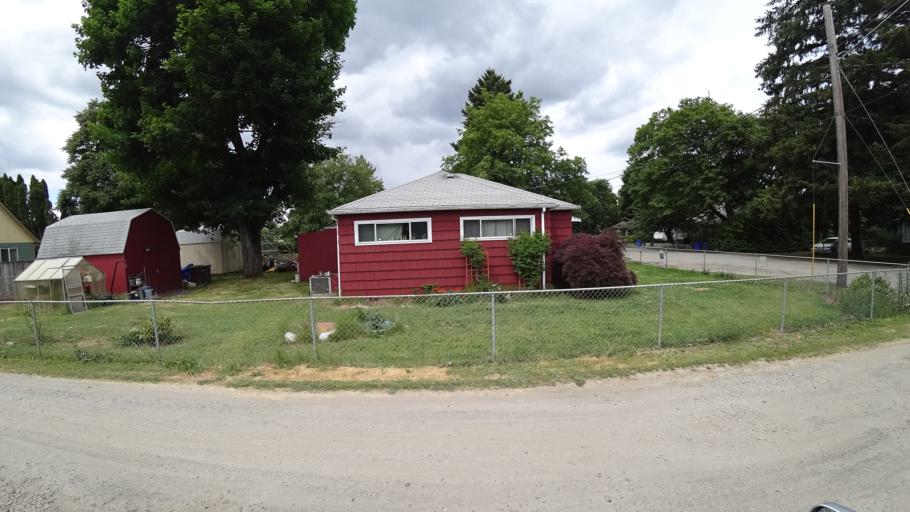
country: US
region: Oregon
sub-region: Clackamas County
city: Happy Valley
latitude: 45.4960
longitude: -122.5167
